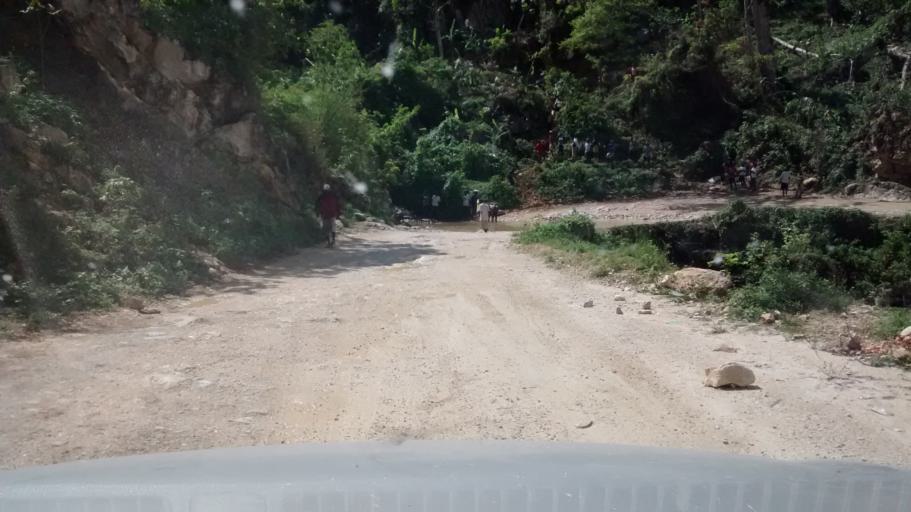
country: HT
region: Grandans
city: Corail
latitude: 18.5107
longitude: -73.9769
